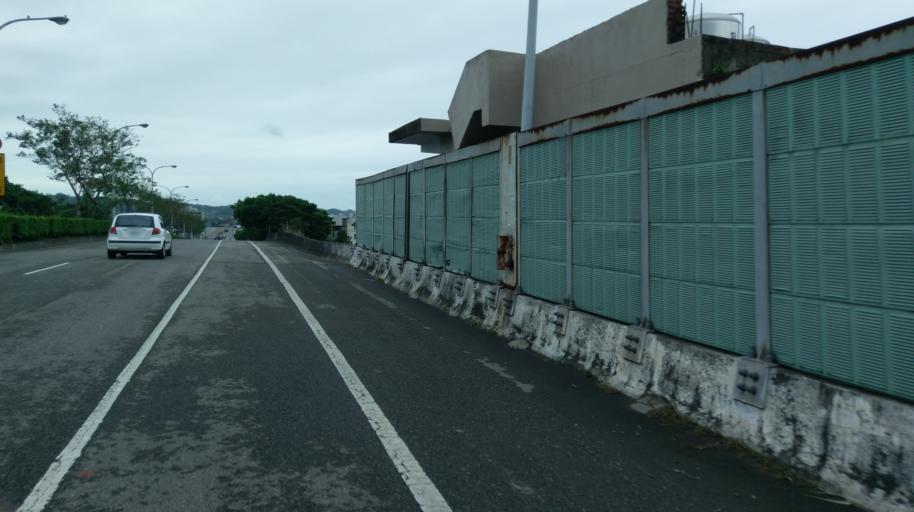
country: TW
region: Taiwan
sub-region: Miaoli
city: Miaoli
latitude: 24.6628
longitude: 120.8815
